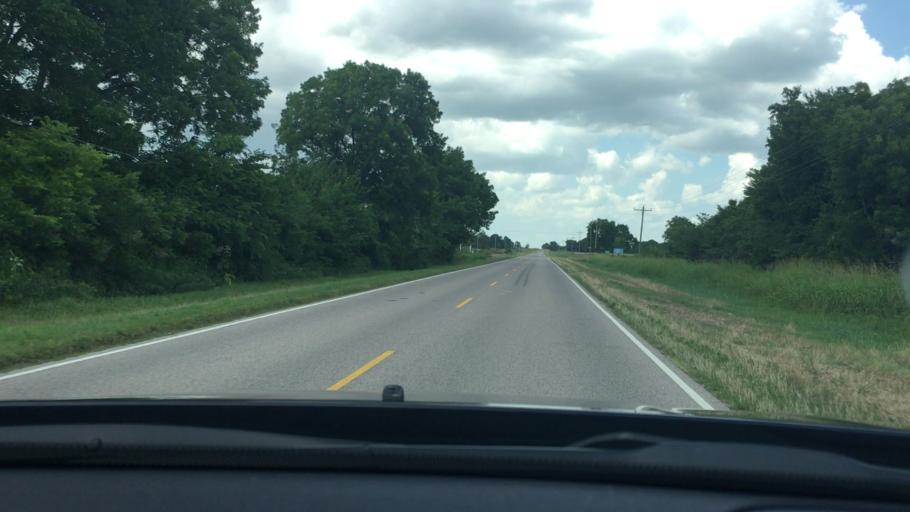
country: US
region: Oklahoma
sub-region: Johnston County
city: Tishomingo
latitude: 34.4608
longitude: -96.6359
